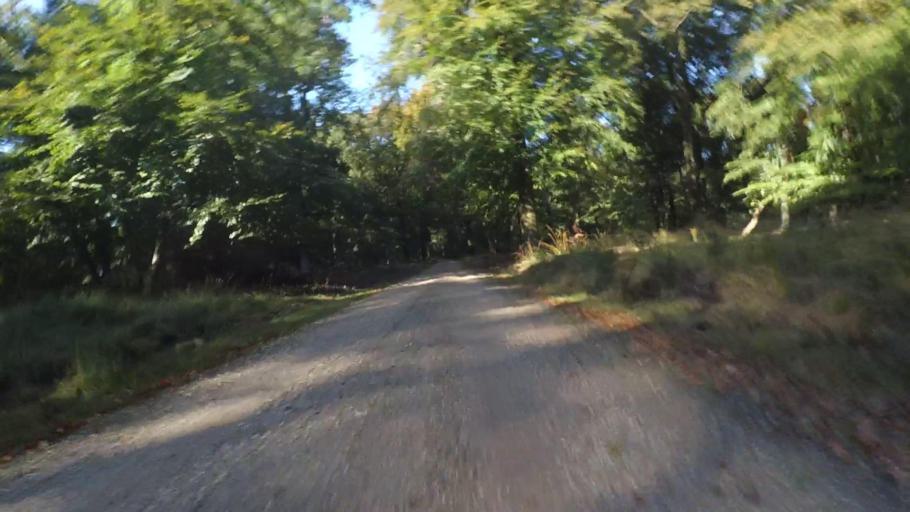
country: NL
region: Gelderland
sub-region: Gemeente Epe
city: Vaassen
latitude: 52.2486
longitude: 5.8771
